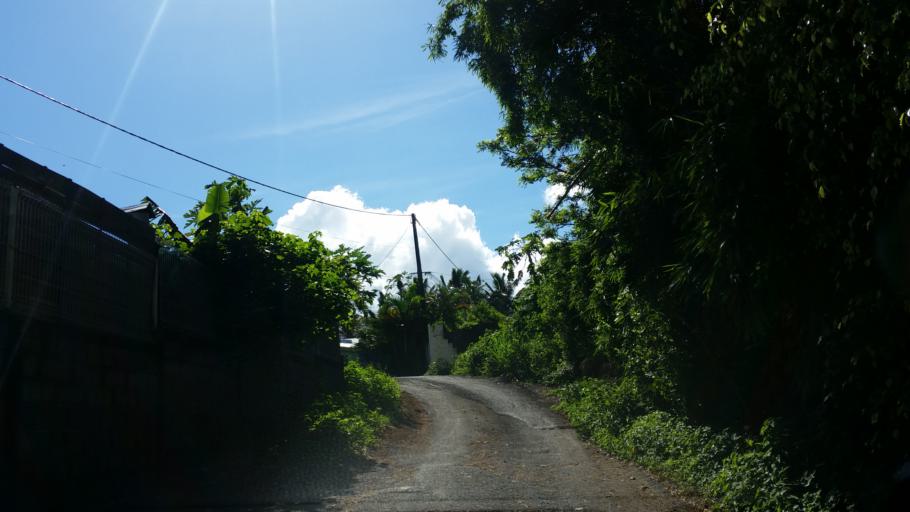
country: RE
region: Reunion
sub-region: Reunion
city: Sainte-Marie
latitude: -20.9229
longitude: 55.5244
